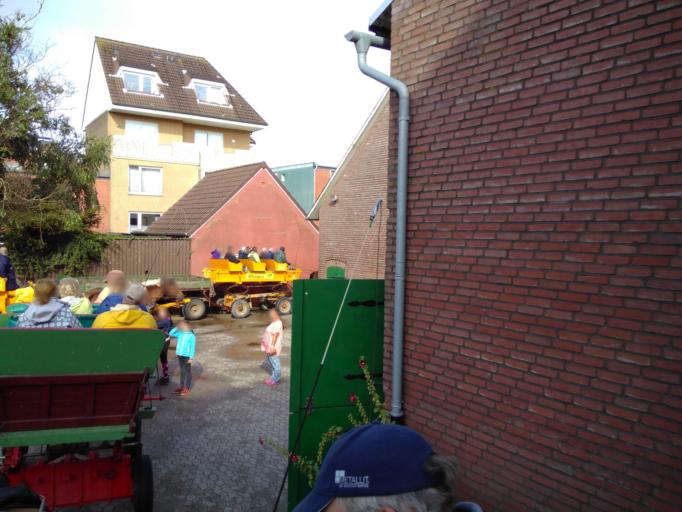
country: DE
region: Lower Saxony
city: Cuxhaven
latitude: 53.8848
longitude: 8.6385
